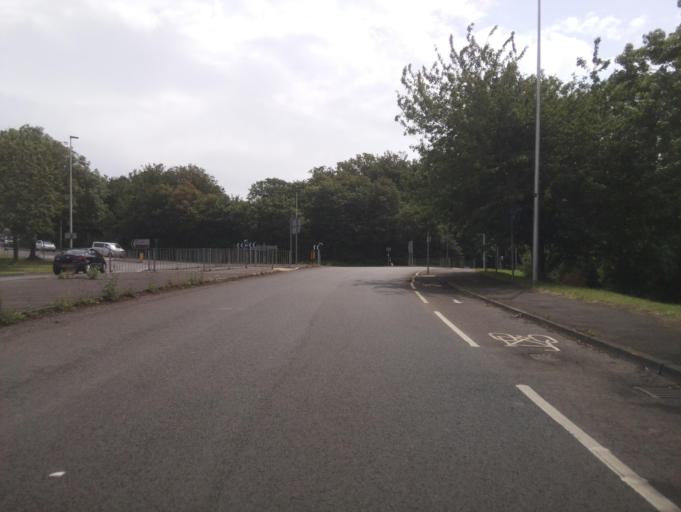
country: GB
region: Wales
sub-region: Vale of Glamorgan
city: Dinas Powys
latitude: 51.4074
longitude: -3.2252
